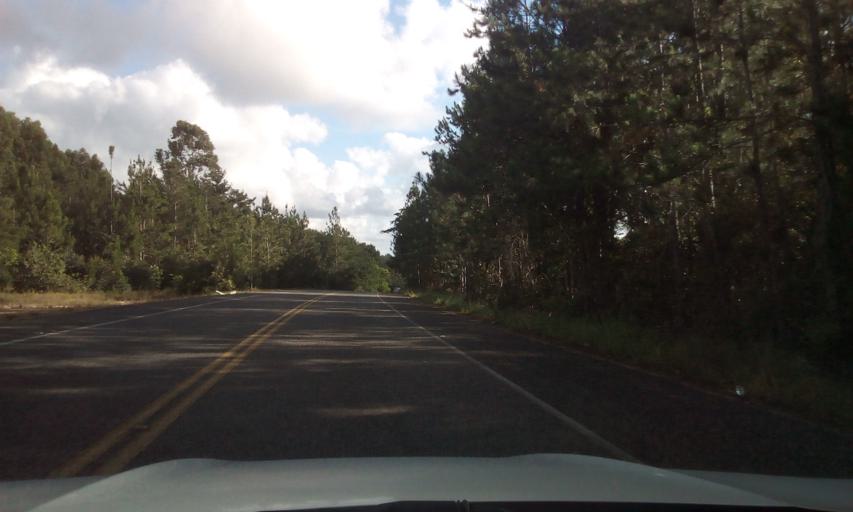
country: BR
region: Bahia
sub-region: Conde
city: Conde
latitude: -12.1040
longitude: -37.7827
